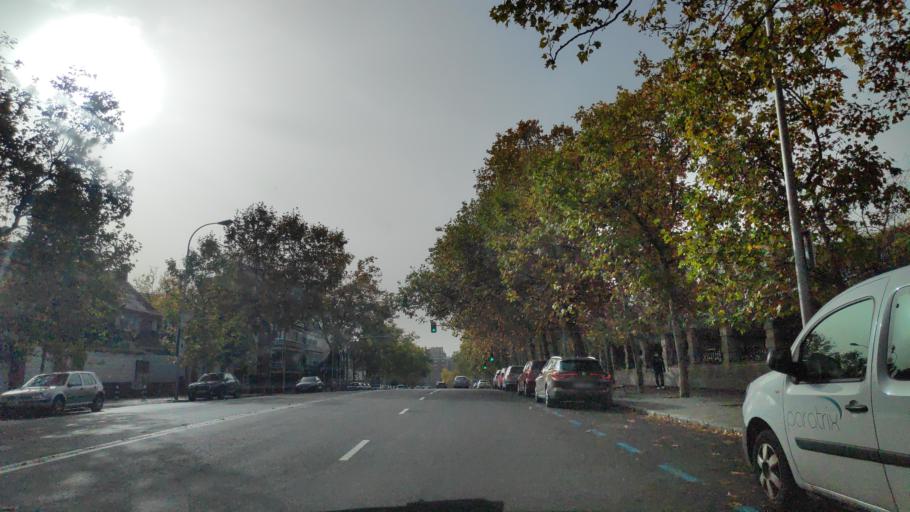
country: ES
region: Madrid
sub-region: Provincia de Madrid
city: Chamartin
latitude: 40.4656
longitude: -3.6857
